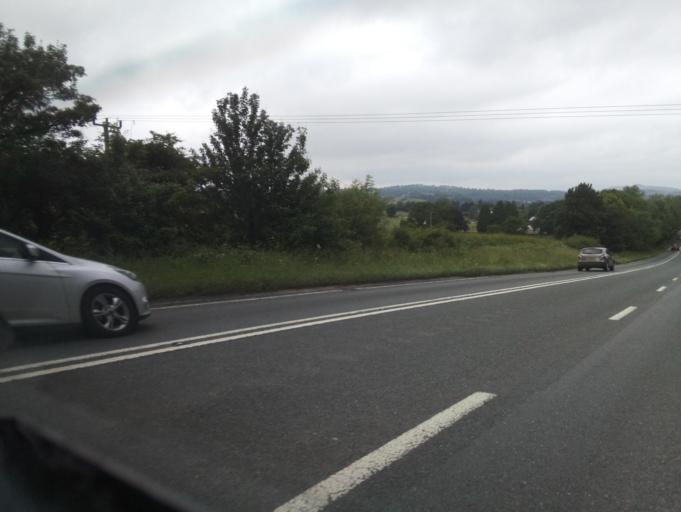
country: GB
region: England
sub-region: Staffordshire
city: Mayfield
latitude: 52.9949
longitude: -1.7490
